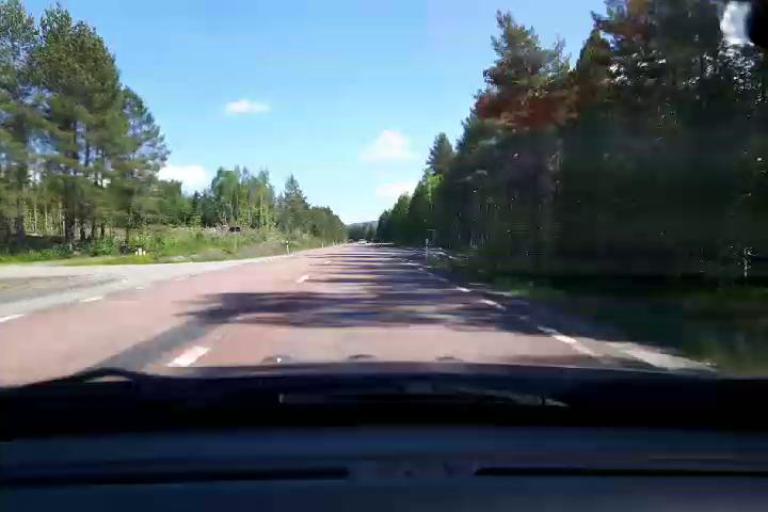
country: SE
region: Gaevleborg
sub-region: Hudiksvalls Kommun
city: Delsbo
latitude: 61.7738
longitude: 16.6762
